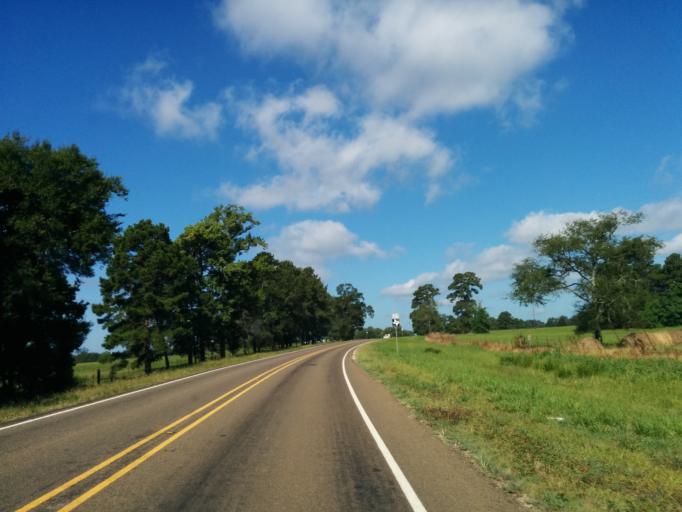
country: US
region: Texas
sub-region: Sabine County
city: Milam
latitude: 31.4131
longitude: -93.9929
